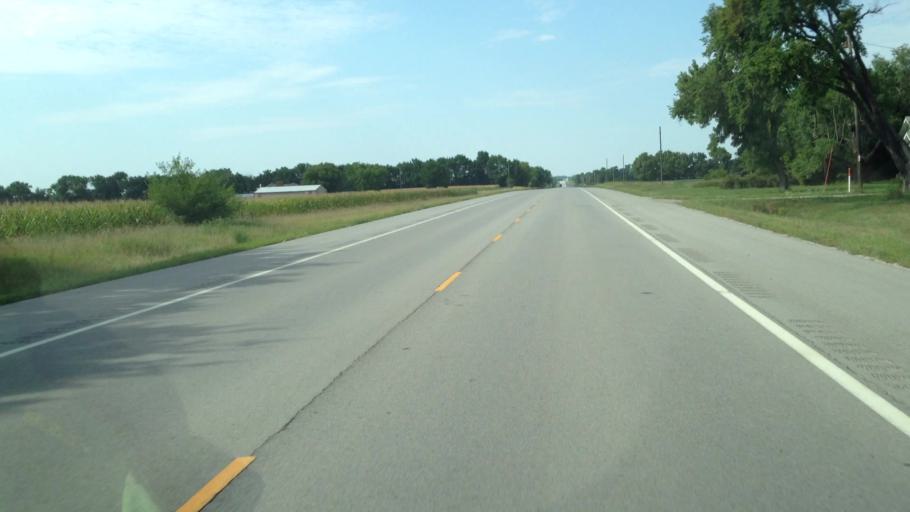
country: US
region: Kansas
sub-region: Labette County
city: Altamont
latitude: 37.2556
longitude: -95.2671
